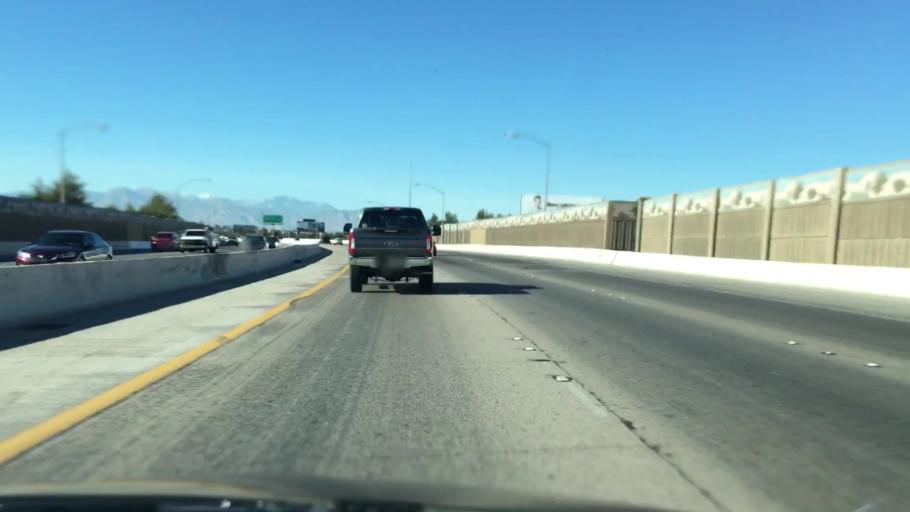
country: US
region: Nevada
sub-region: Clark County
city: North Las Vegas
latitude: 36.1665
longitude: -115.0973
